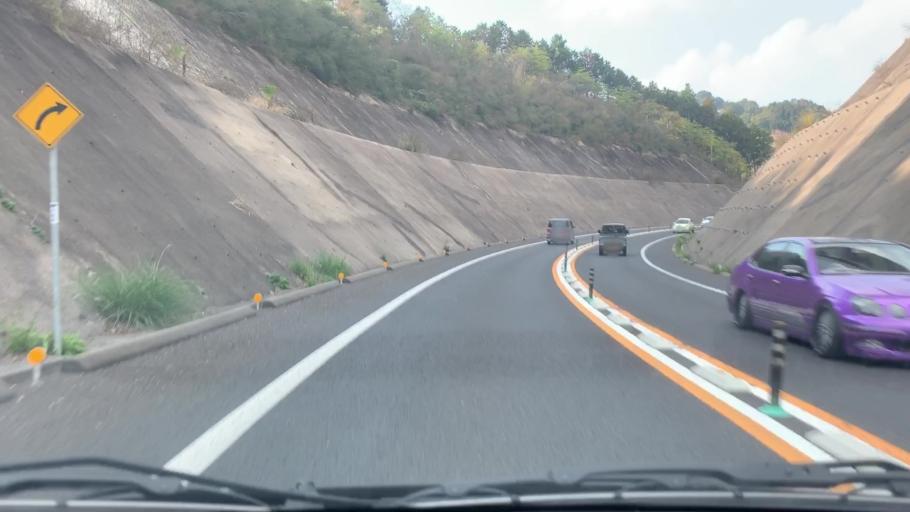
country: JP
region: Nagasaki
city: Sasebo
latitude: 32.9962
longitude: 129.7299
